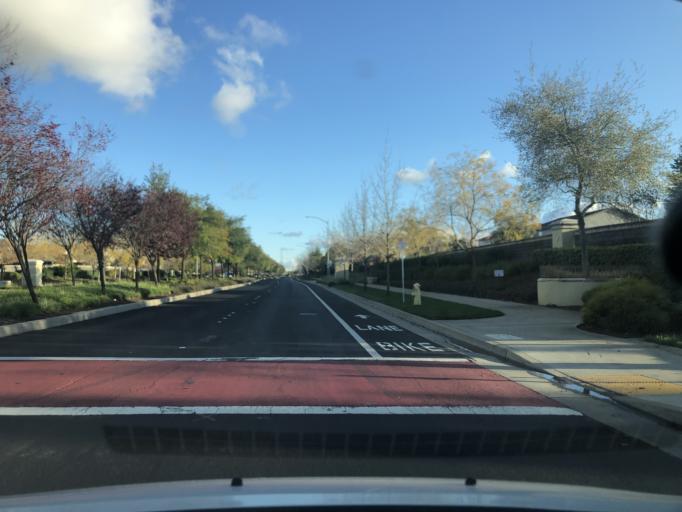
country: US
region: California
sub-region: Sacramento County
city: Antelope
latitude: 38.7698
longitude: -121.3668
